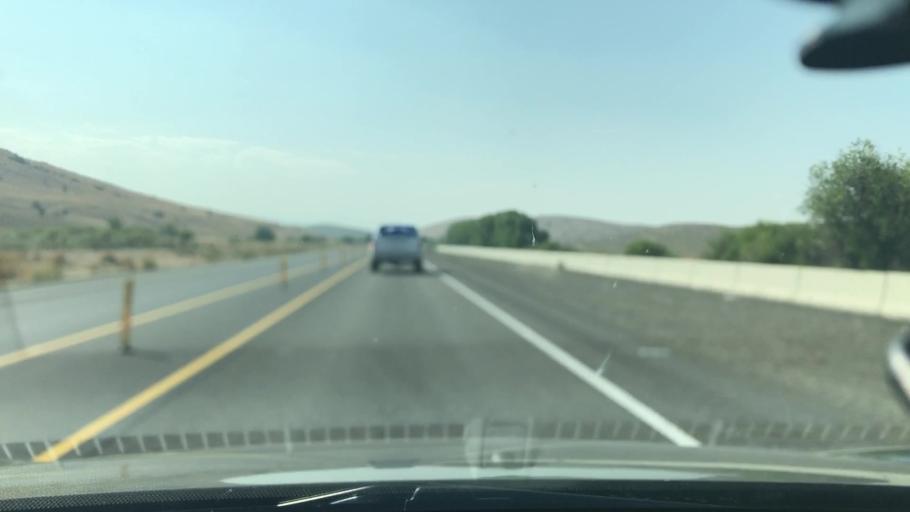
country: US
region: Oregon
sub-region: Baker County
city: Baker City
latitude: 44.6753
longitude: -117.6387
